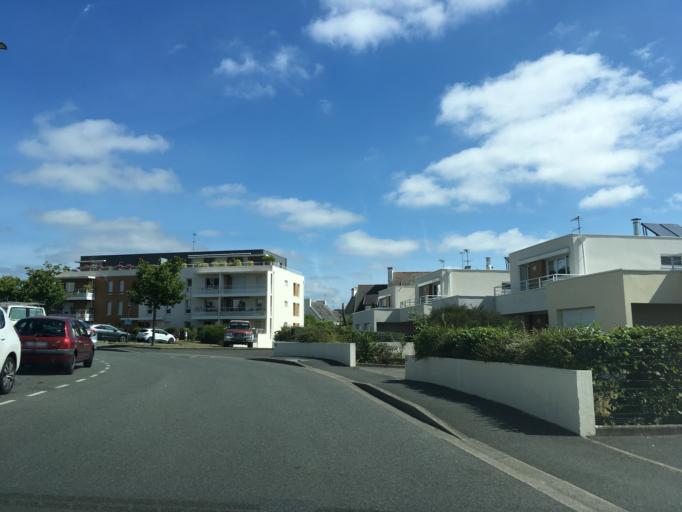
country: FR
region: Brittany
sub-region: Departement du Finistere
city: Quimper
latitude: 48.0066
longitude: -4.0938
